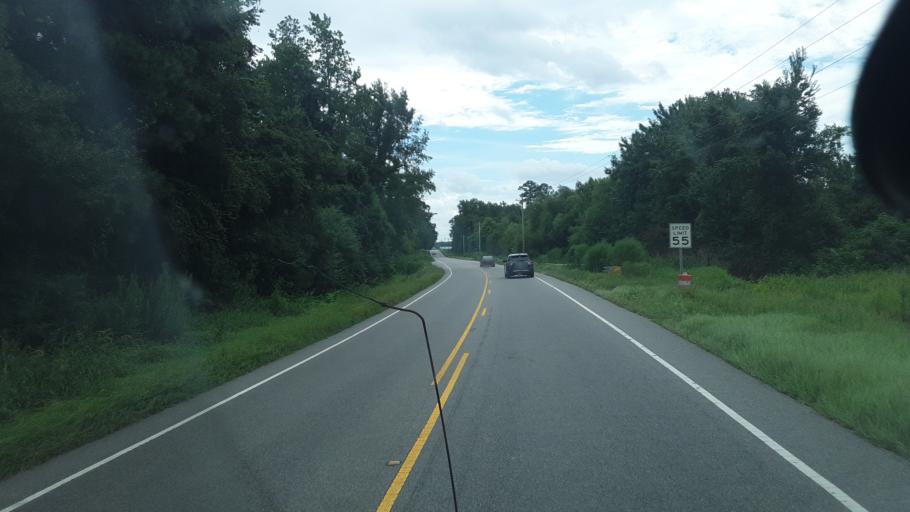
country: US
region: North Carolina
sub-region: Robeson County
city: Rowland
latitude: 34.5901
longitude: -79.3250
